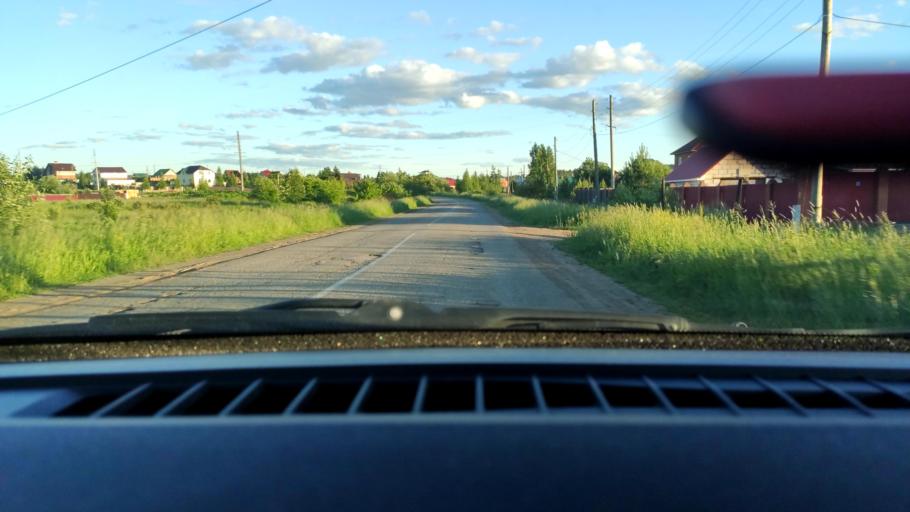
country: RU
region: Perm
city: Kultayevo
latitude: 57.9315
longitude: 55.8631
